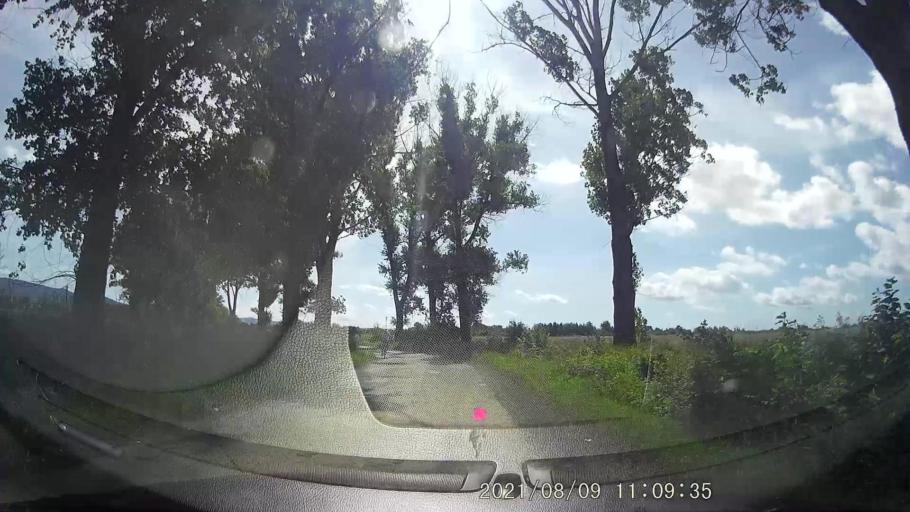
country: PL
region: Lower Silesian Voivodeship
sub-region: Powiat klodzki
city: Klodzko
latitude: 50.4507
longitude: 16.6175
